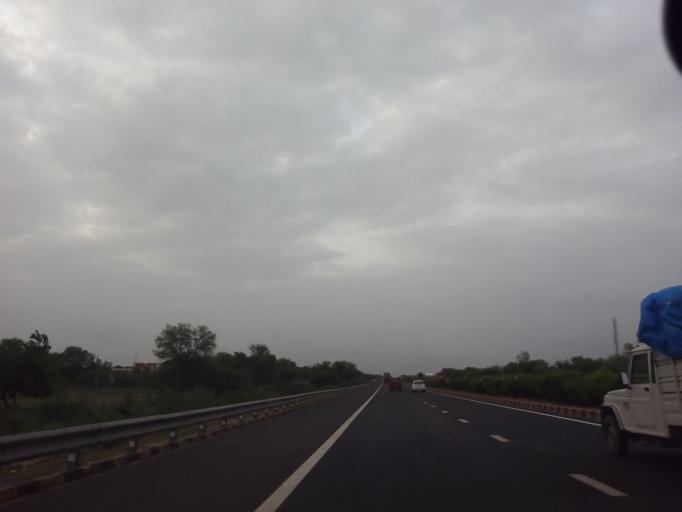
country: IN
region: Gujarat
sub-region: Kheda
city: Mahemdavad
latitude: 22.9101
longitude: 72.7661
